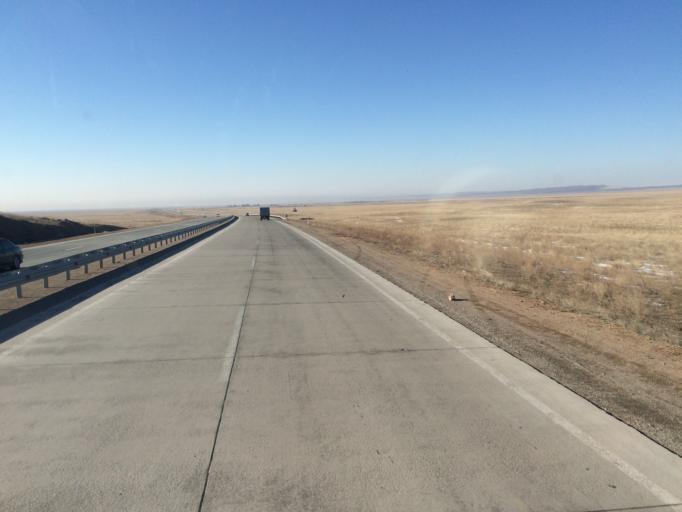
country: KZ
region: Zhambyl
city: Georgiyevka
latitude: 43.3426
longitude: 74.4459
